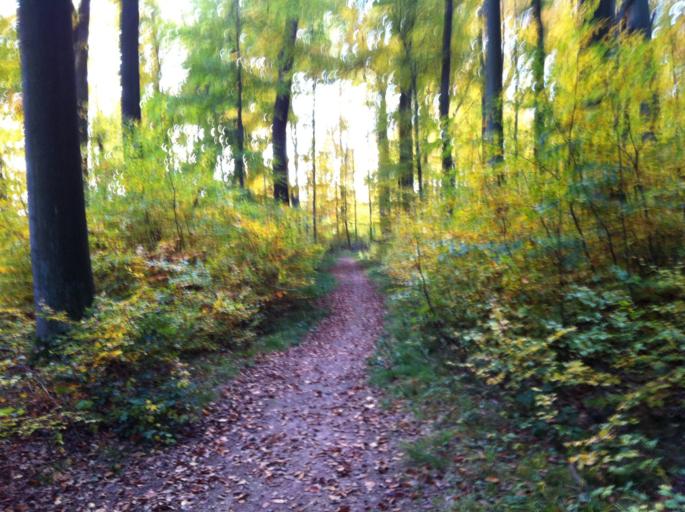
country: DE
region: Hesse
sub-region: Regierungsbezirk Darmstadt
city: Wiesbaden
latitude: 50.1048
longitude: 8.2327
